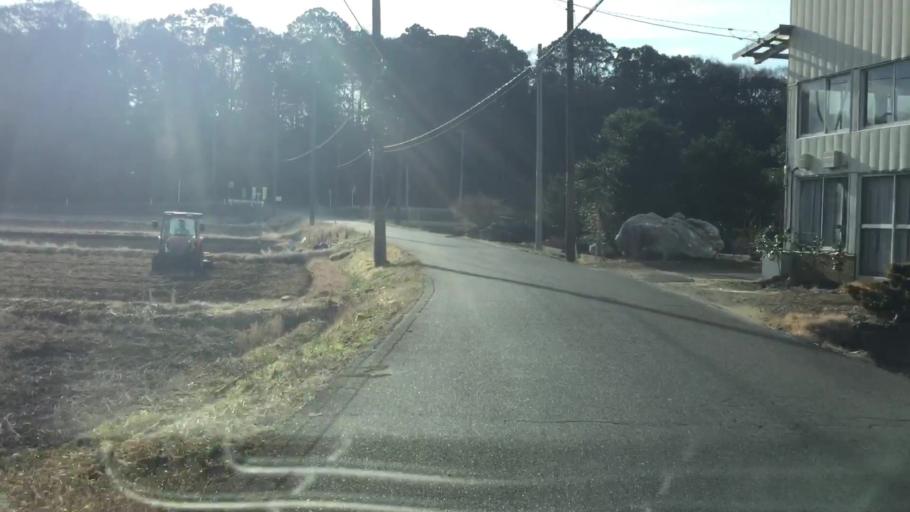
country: JP
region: Chiba
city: Shiroi
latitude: 35.8249
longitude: 140.1218
